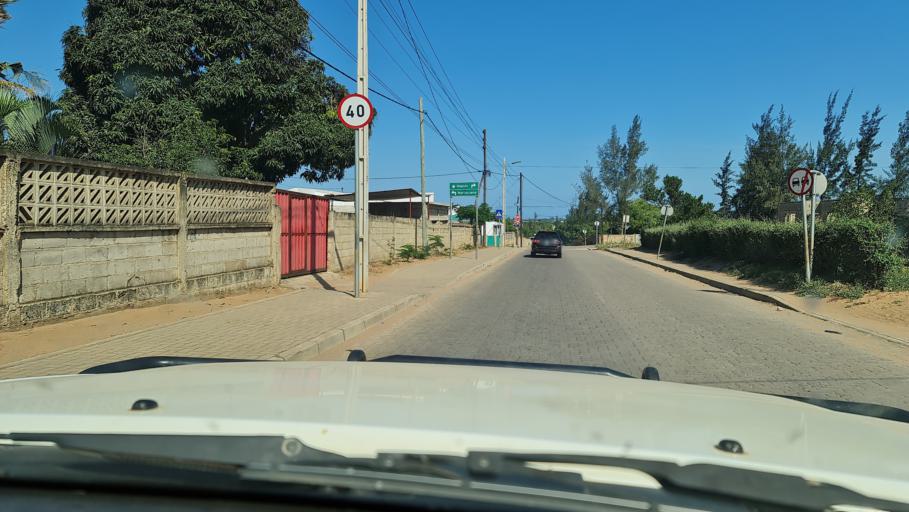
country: MZ
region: Maputo City
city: Maputo
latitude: -25.8424
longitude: 32.6423
